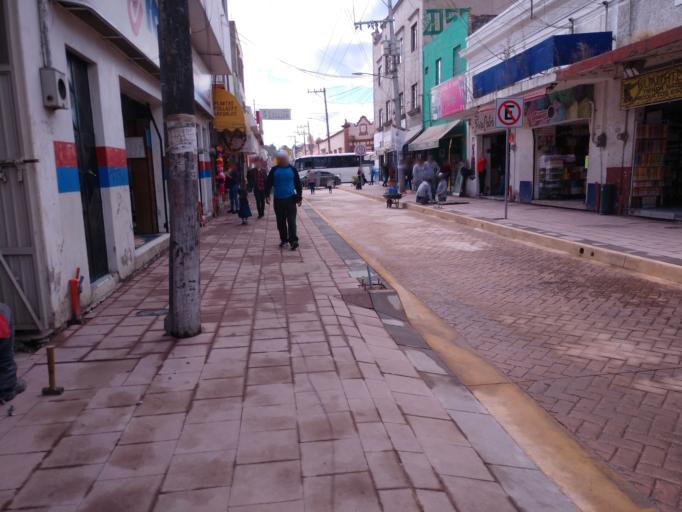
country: MX
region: Nayarit
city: Tepic
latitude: 21.5128
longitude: -104.8938
